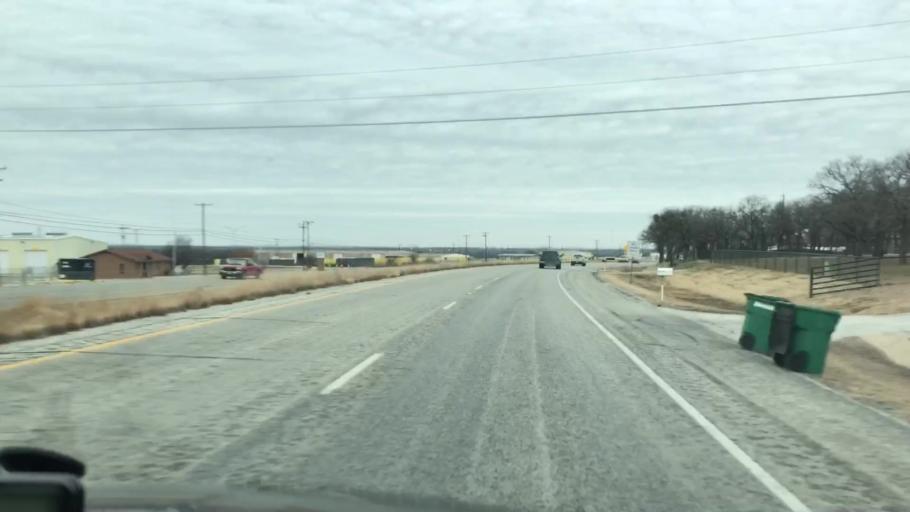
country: US
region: Texas
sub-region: Jack County
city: Jacksboro
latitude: 33.1948
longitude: -98.1440
